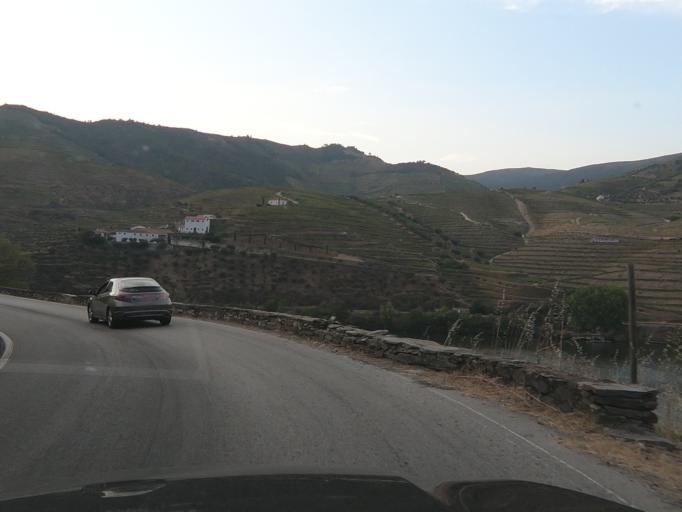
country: PT
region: Viseu
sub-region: Tabuaco
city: Tabuaco
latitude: 41.1645
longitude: -7.5694
